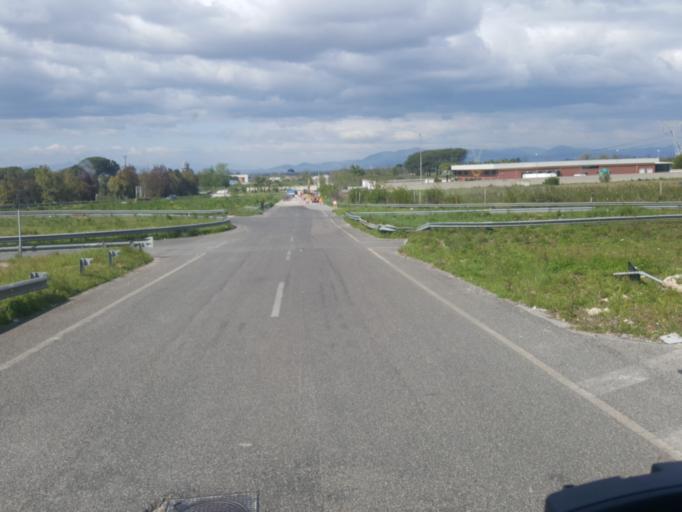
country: IT
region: Campania
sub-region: Provincia di Napoli
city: Torretta-Scalzapecora
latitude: 40.9313
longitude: 14.1225
